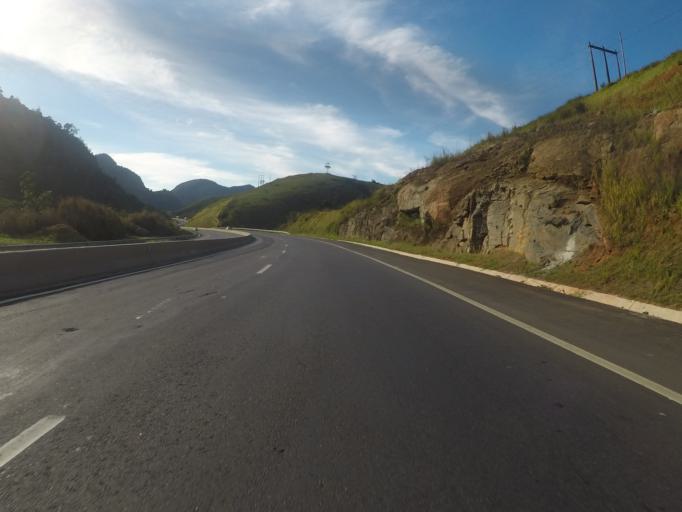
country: BR
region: Espirito Santo
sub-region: Ibiracu
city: Ibiracu
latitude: -19.8547
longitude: -40.3822
